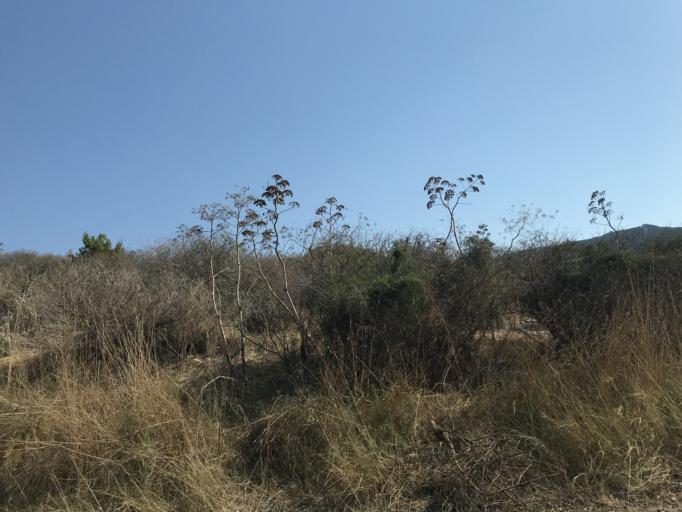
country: TR
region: Izmir
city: Selcuk
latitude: 37.9475
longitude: 27.3425
